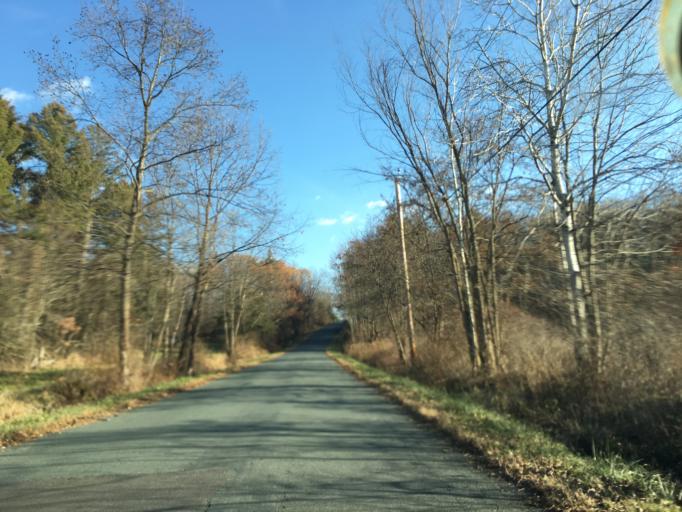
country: US
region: New York
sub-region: Rensselaer County
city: West Sand Lake
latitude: 42.6013
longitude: -73.5963
